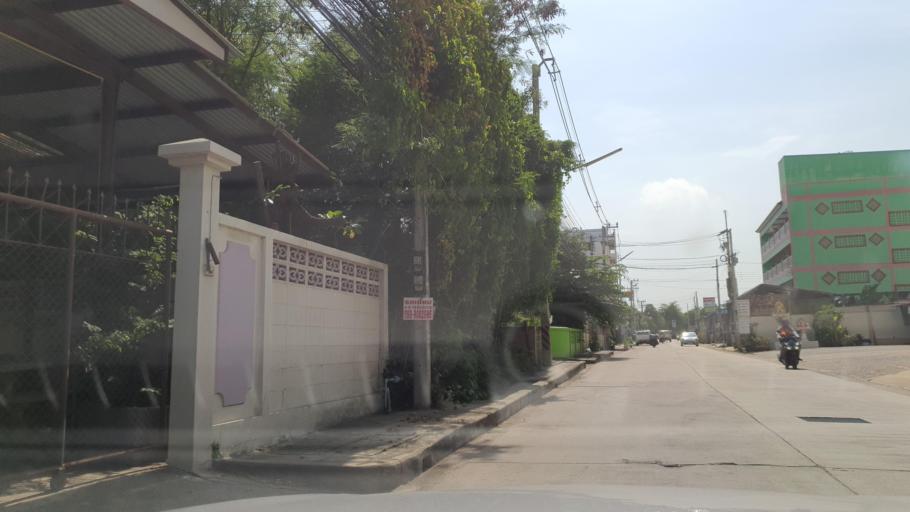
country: TH
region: Chachoengsao
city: Chachoengsao
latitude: 13.6807
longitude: 101.0665
